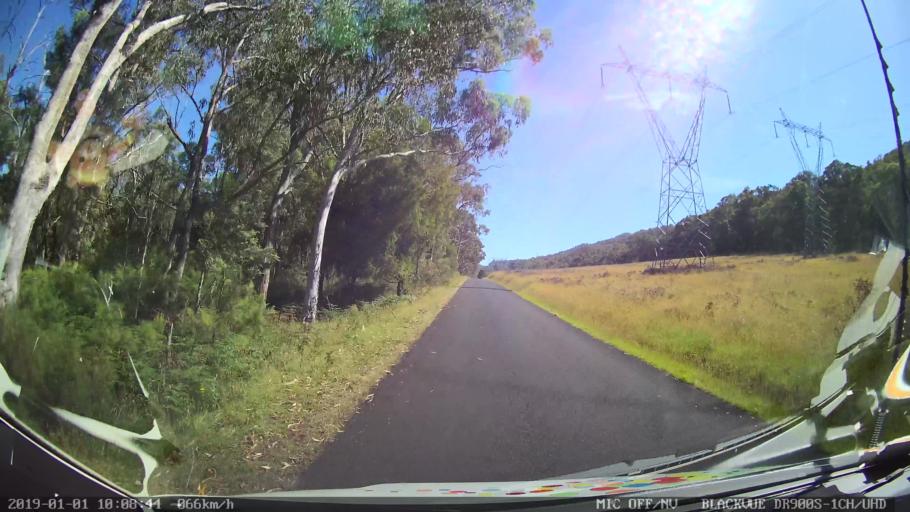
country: AU
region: New South Wales
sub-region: Snowy River
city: Jindabyne
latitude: -36.1564
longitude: 148.1578
